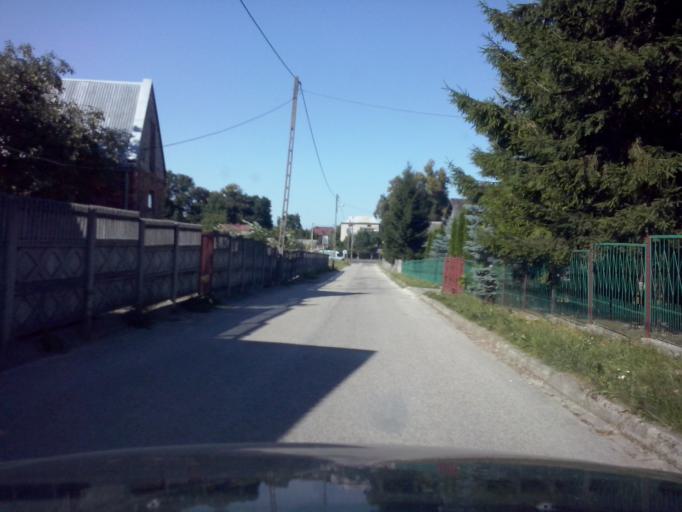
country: PL
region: Swietokrzyskie
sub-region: Powiat kielecki
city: Chmielnik
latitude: 50.6105
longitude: 20.7337
